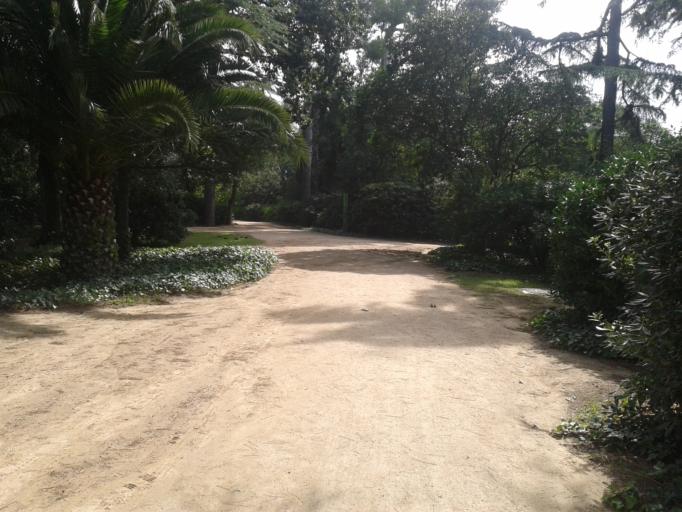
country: ES
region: Catalonia
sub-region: Provincia de Barcelona
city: les Corts
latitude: 41.3873
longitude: 2.1165
